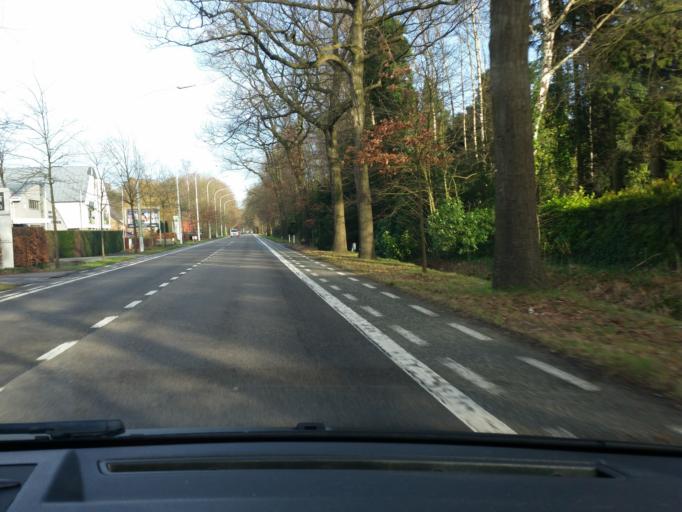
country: BE
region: Flanders
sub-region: Provincie Antwerpen
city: Brasschaat
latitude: 51.3386
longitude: 4.5287
